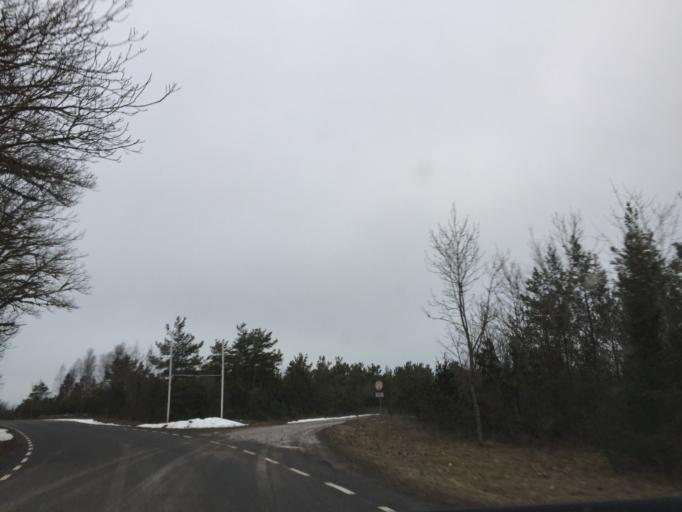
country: EE
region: Saare
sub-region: Kuressaare linn
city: Kuressaare
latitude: 58.5623
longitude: 22.3139
